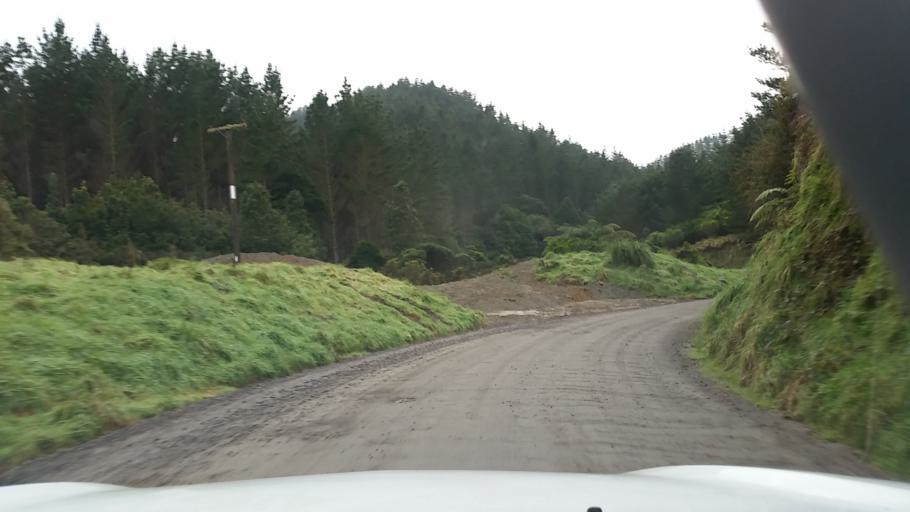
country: NZ
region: Taranaki
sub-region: South Taranaki District
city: Eltham
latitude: -39.5219
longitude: 174.4160
